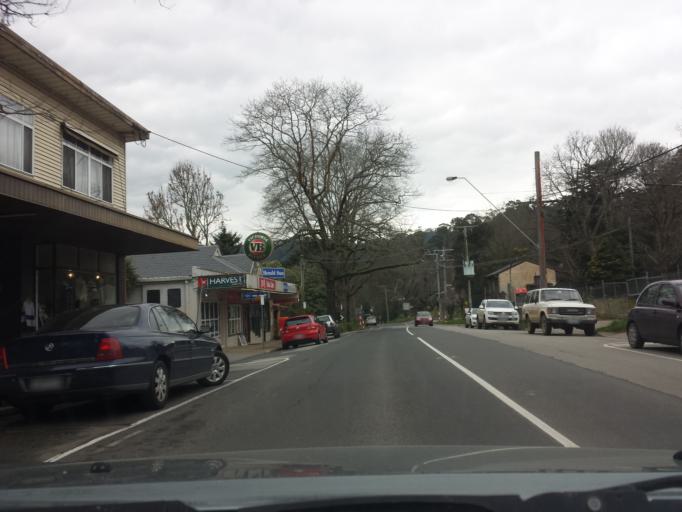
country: AU
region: Victoria
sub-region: Yarra Ranges
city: Kallista
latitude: -37.8844
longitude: 145.3695
